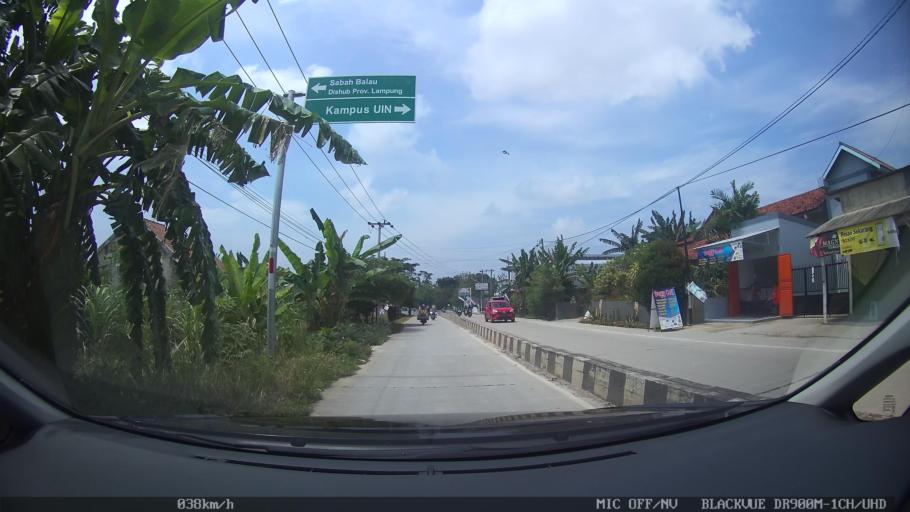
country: ID
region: Lampung
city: Kedaton
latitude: -5.3746
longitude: 105.3101
